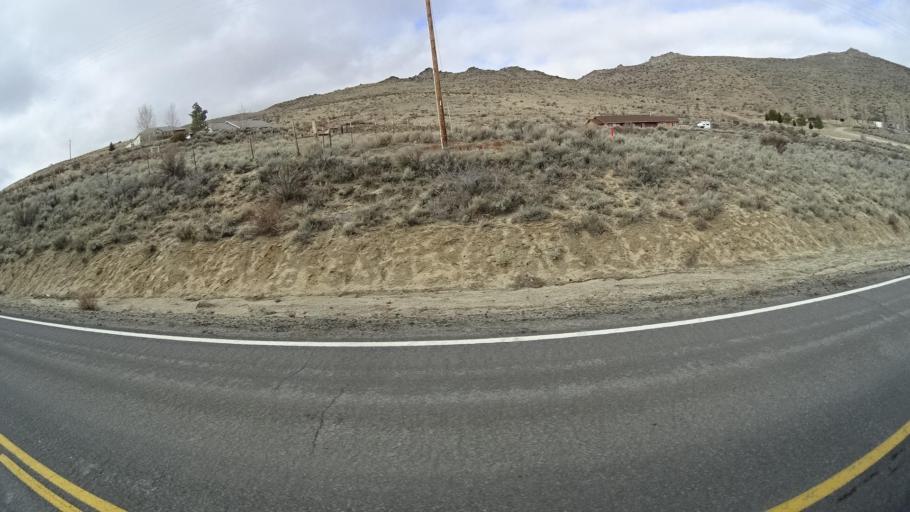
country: US
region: Nevada
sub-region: Washoe County
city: Cold Springs
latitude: 39.8457
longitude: -119.9351
